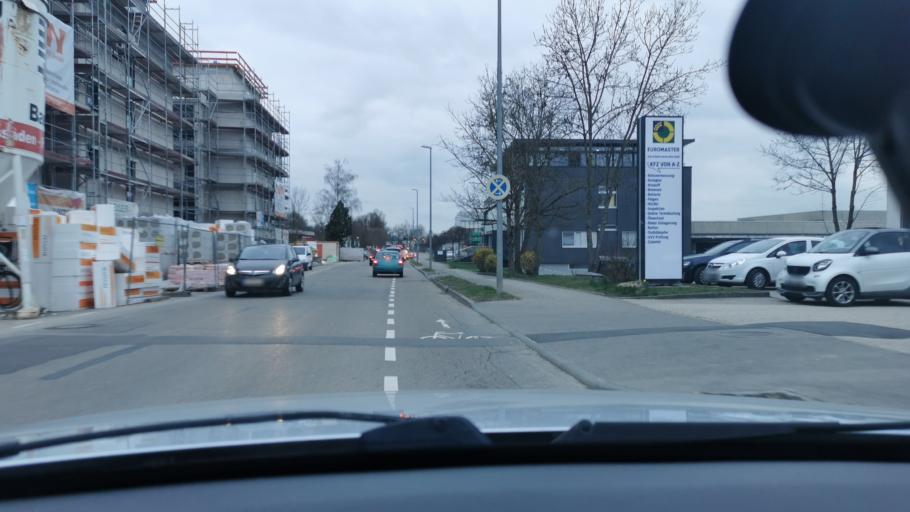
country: DE
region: Baden-Wuerttemberg
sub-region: Regierungsbezirk Stuttgart
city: Kirchheim unter Teck
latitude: 48.6480
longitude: 9.4341
